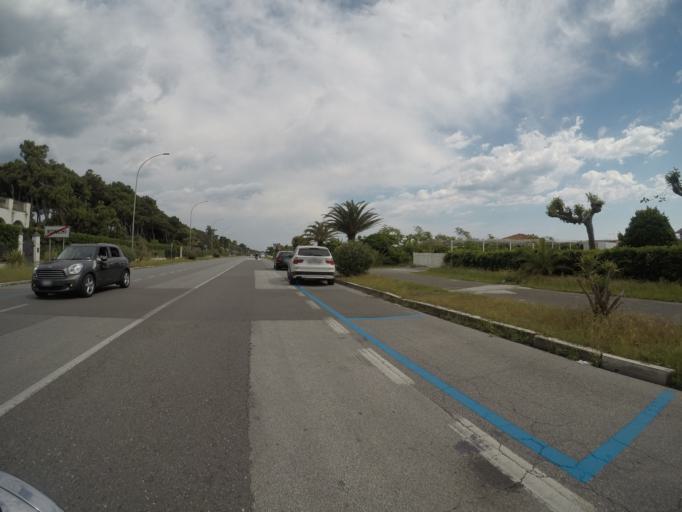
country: IT
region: Tuscany
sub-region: Provincia di Massa-Carrara
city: Massa
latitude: 43.9946
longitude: 10.1202
